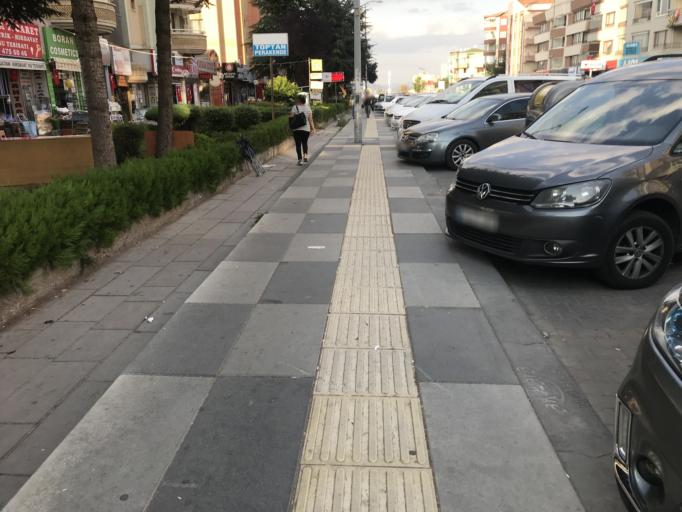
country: TR
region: Ankara
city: Ankara
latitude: 39.8704
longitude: 32.8281
